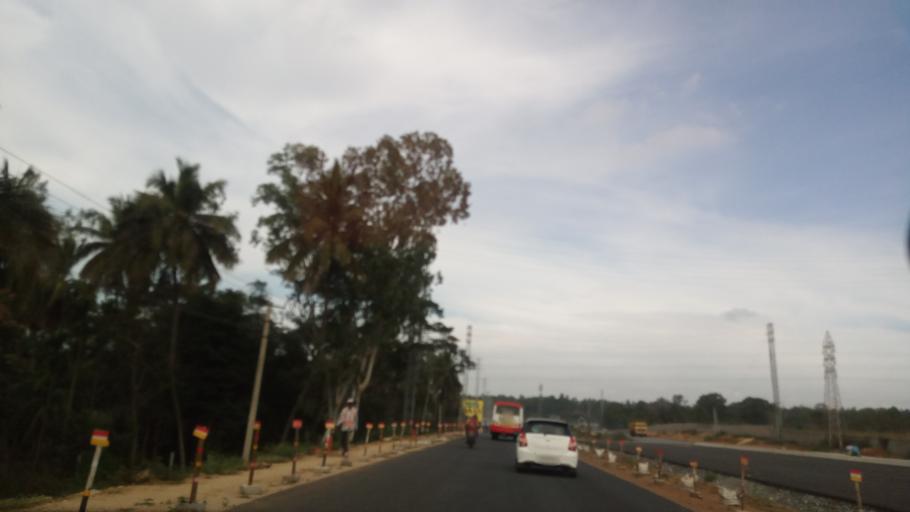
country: IN
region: Karnataka
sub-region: Mandya
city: Shrirangapattana
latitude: 12.4428
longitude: 76.7295
